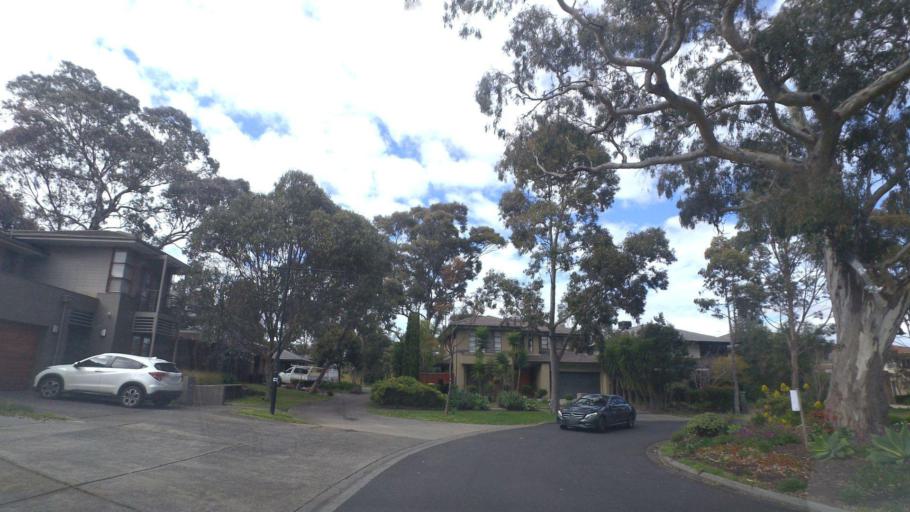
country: AU
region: Victoria
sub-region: Banyule
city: Bundoora
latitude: -37.7161
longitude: 145.0603
